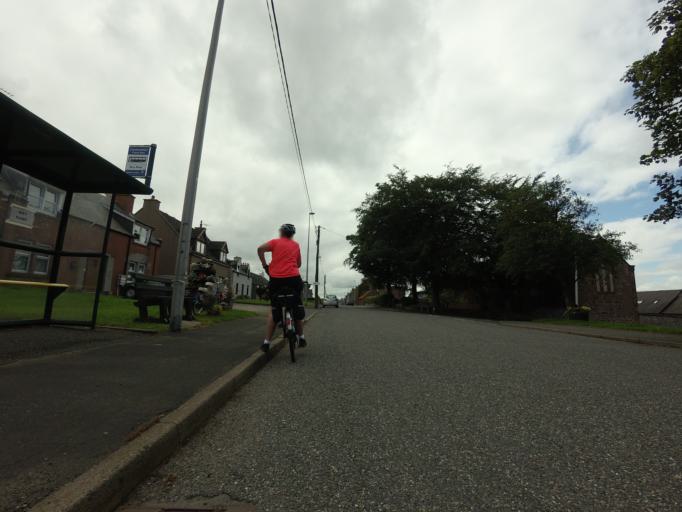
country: GB
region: Scotland
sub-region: Aberdeenshire
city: Turriff
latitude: 57.5433
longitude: -2.3251
